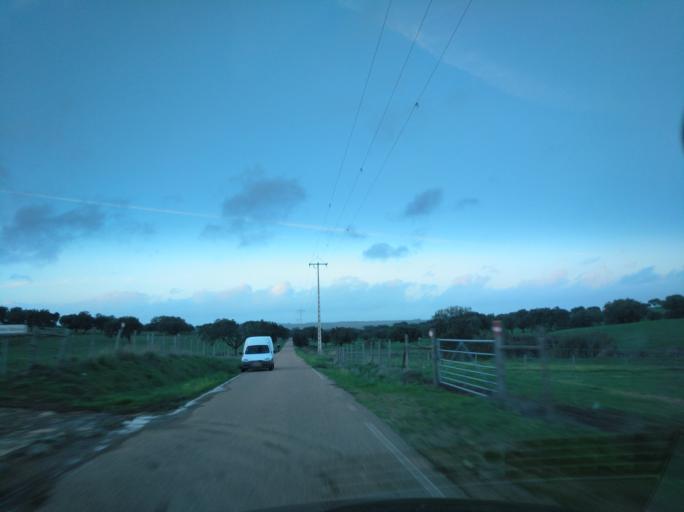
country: PT
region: Portalegre
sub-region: Campo Maior
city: Campo Maior
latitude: 39.0776
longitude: -7.1163
